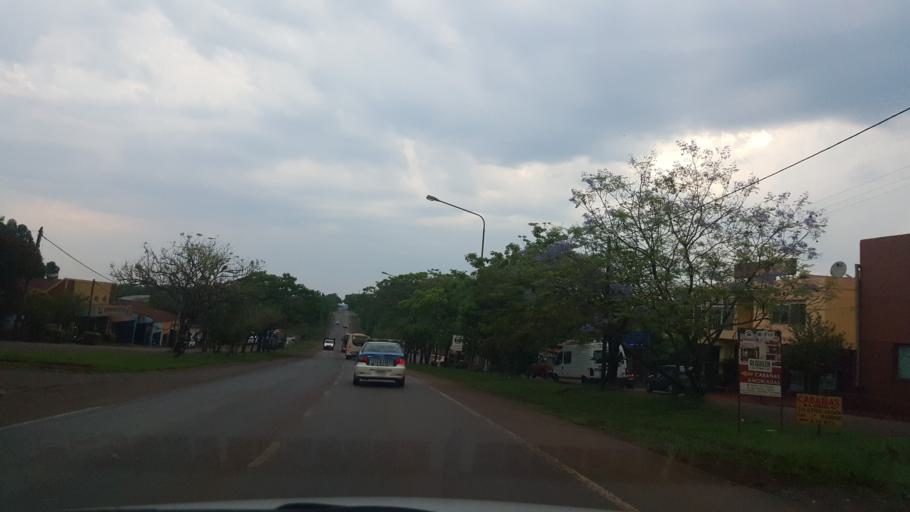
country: AR
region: Misiones
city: Jardin America
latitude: -27.0427
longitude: -55.2340
